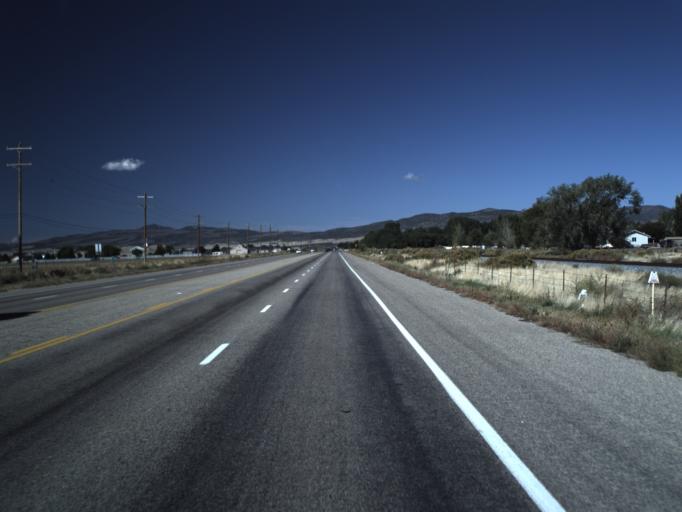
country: US
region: Utah
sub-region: Iron County
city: Cedar City
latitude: 37.6851
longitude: -113.1237
